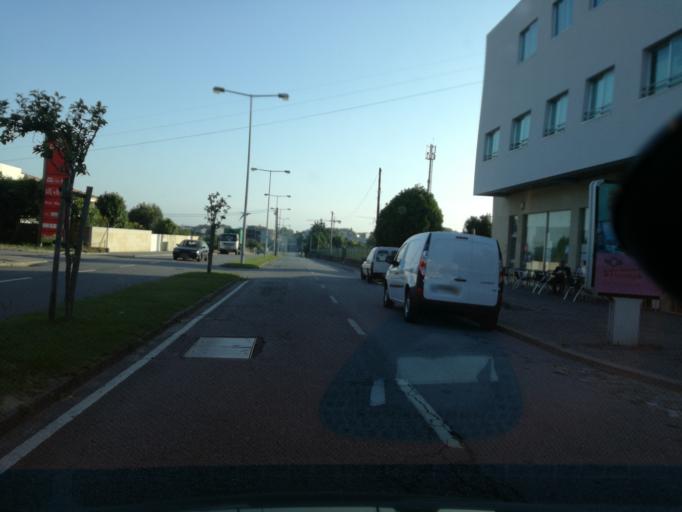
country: PT
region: Porto
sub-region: Maia
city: Leca do Bailio
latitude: 41.2176
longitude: -8.6044
